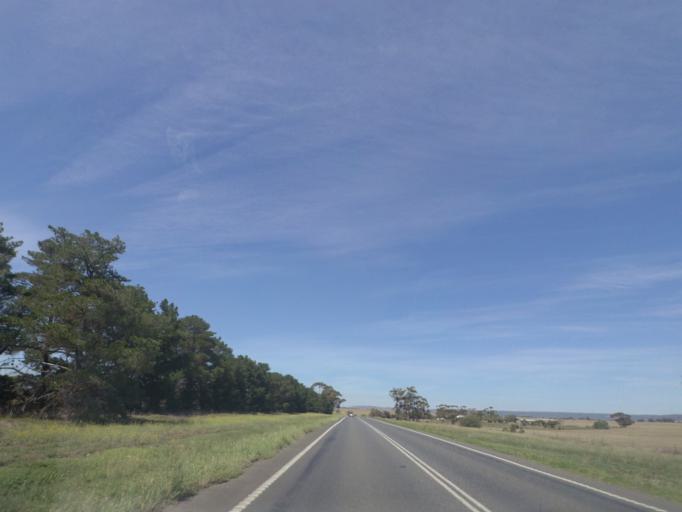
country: AU
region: Victoria
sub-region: Moorabool
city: Bacchus Marsh
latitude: -37.7980
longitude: 144.4101
